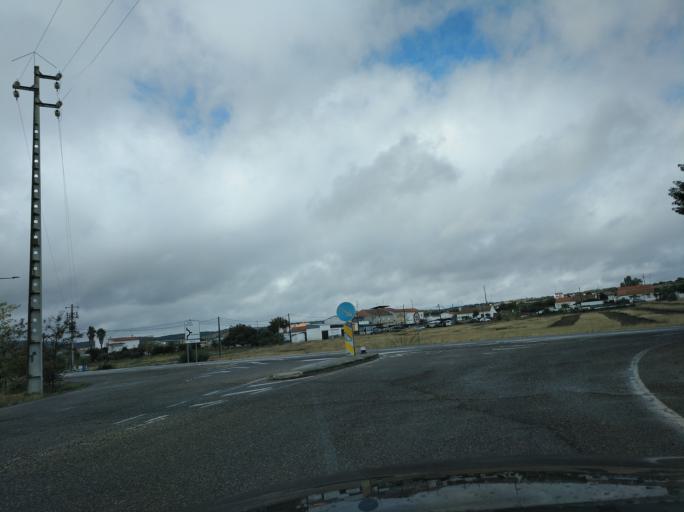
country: PT
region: Portalegre
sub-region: Elvas
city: Elvas
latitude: 38.8880
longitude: -7.1178
